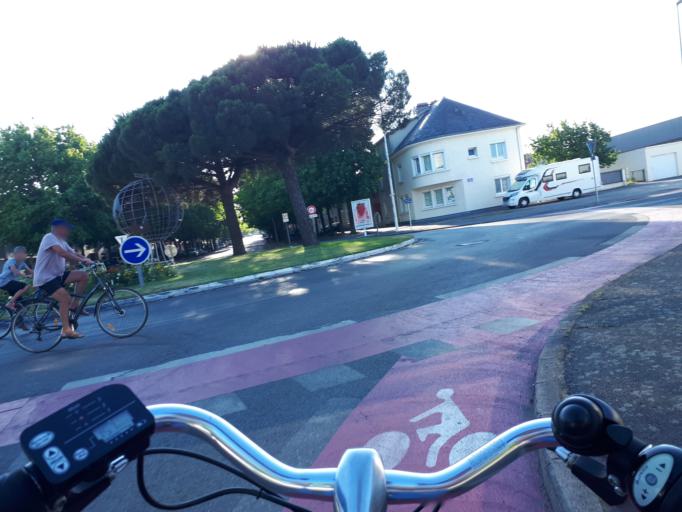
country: FR
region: Pays de la Loire
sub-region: Departement de la Loire-Atlantique
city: Saint-Nazaire
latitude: 47.2821
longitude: -2.2036
